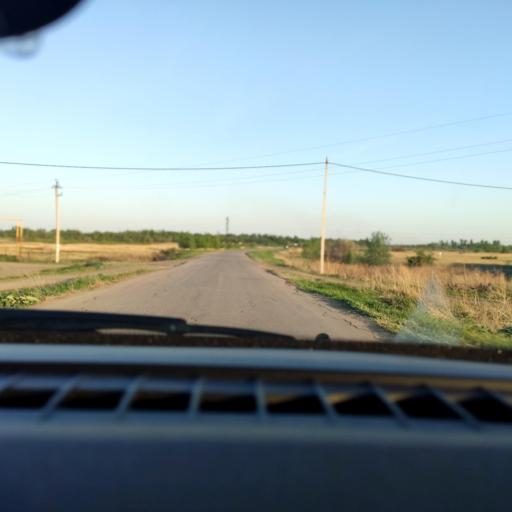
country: RU
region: Samara
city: Georgiyevka
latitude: 53.2690
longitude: 50.9596
